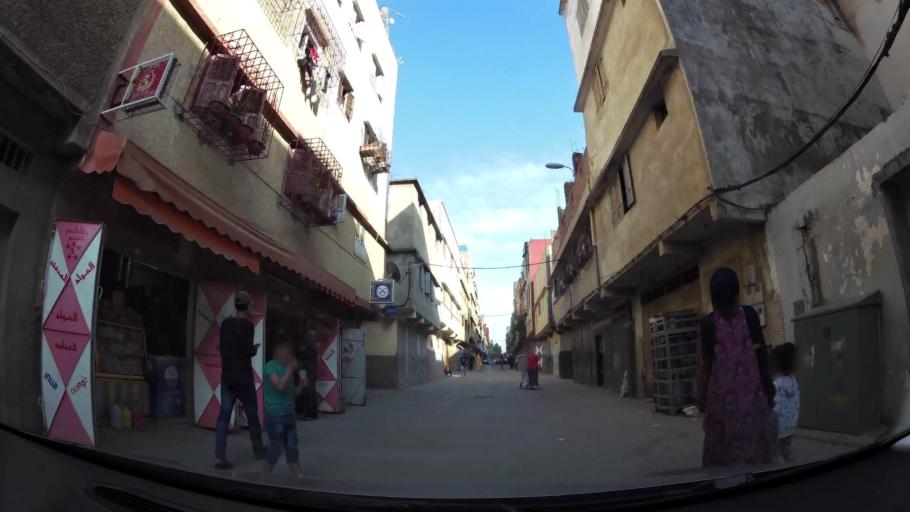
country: MA
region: Rabat-Sale-Zemmour-Zaer
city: Sale
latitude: 34.0544
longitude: -6.7748
